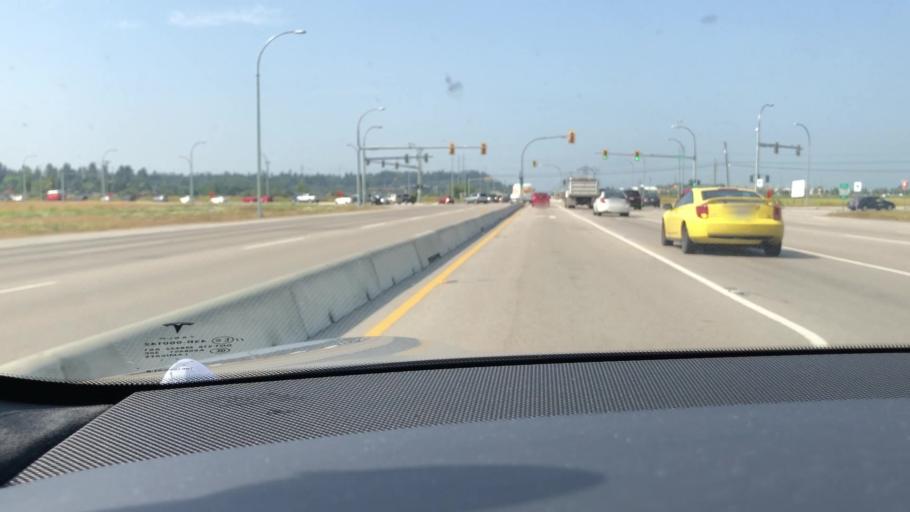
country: CA
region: British Columbia
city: Ladner
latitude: 49.0434
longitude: -123.0675
